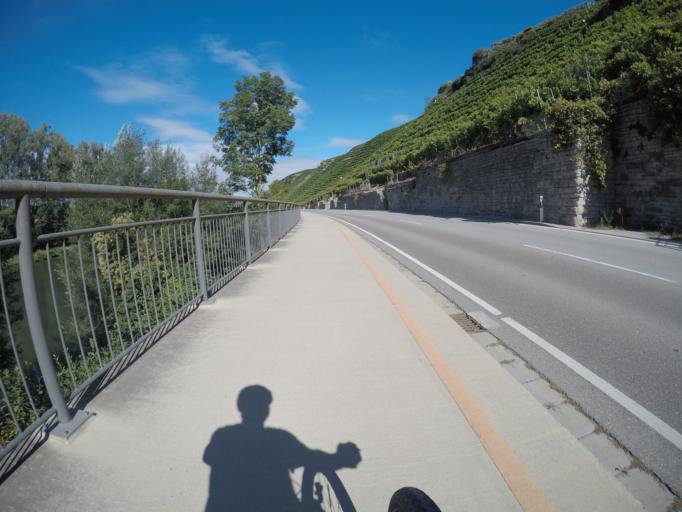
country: DE
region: Baden-Wuerttemberg
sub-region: Regierungsbezirk Stuttgart
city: Mundelsheim
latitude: 48.9803
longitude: 9.2161
